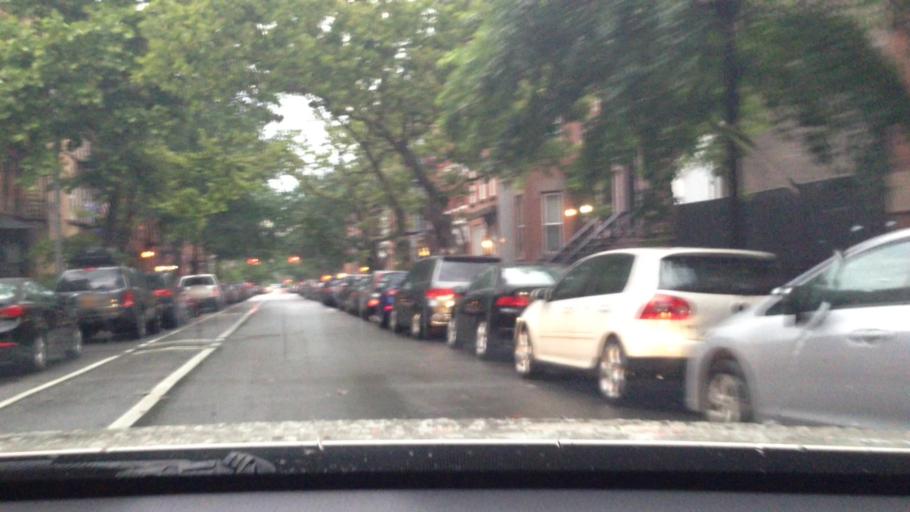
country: US
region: New York
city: New York City
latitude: 40.6837
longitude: -73.9977
